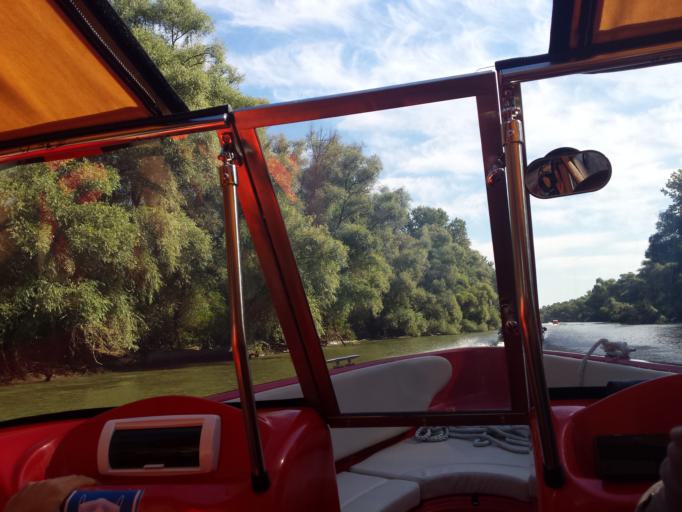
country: RO
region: Tulcea
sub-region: Comuna Nufaru
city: Nufaru
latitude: 45.2177
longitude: 28.8736
